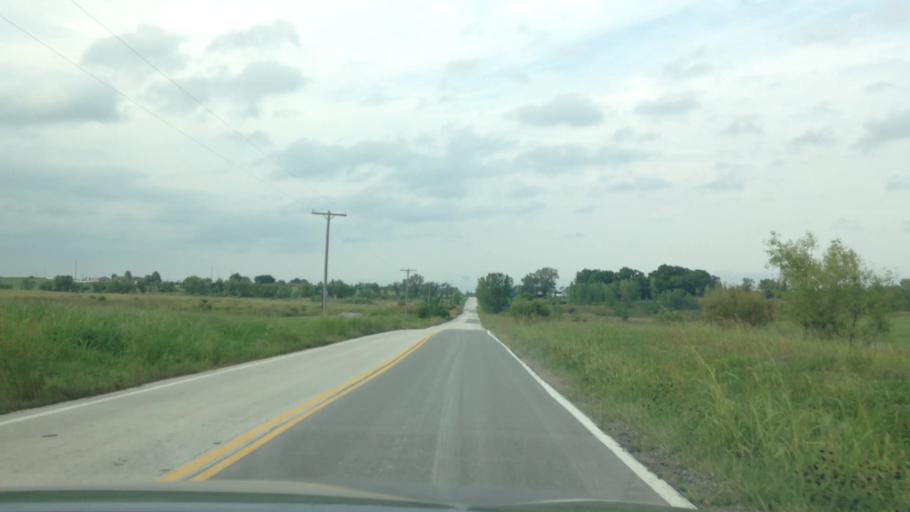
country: US
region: Missouri
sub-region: Platte County
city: Platte City
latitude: 39.3493
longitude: -94.6795
